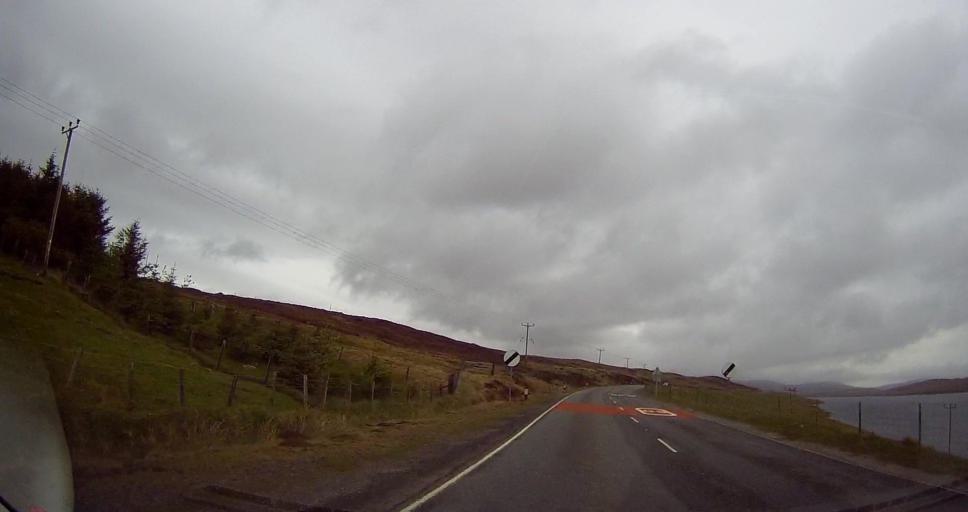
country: GB
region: Scotland
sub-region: Shetland Islands
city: Lerwick
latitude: 60.2415
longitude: -1.2286
